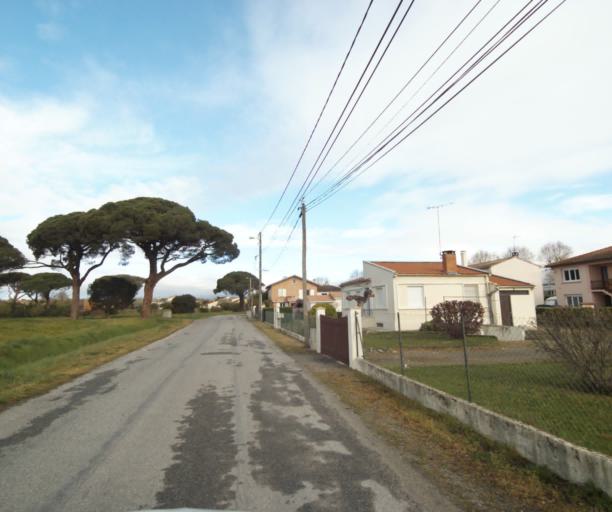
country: FR
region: Midi-Pyrenees
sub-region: Departement de l'Ariege
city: Saverdun
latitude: 43.2314
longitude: 1.5840
